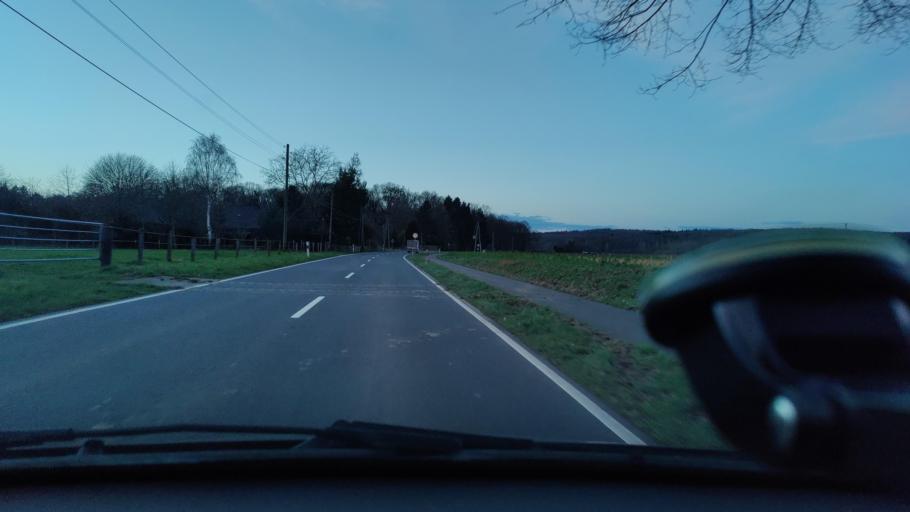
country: DE
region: North Rhine-Westphalia
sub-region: Regierungsbezirk Dusseldorf
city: Xanten
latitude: 51.6203
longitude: 6.4534
